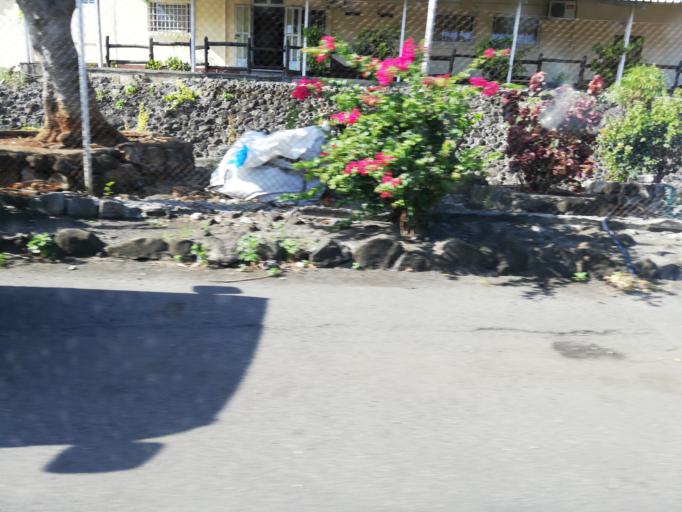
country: MU
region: Port Louis
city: Port Louis
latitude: -20.1609
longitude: 57.4922
